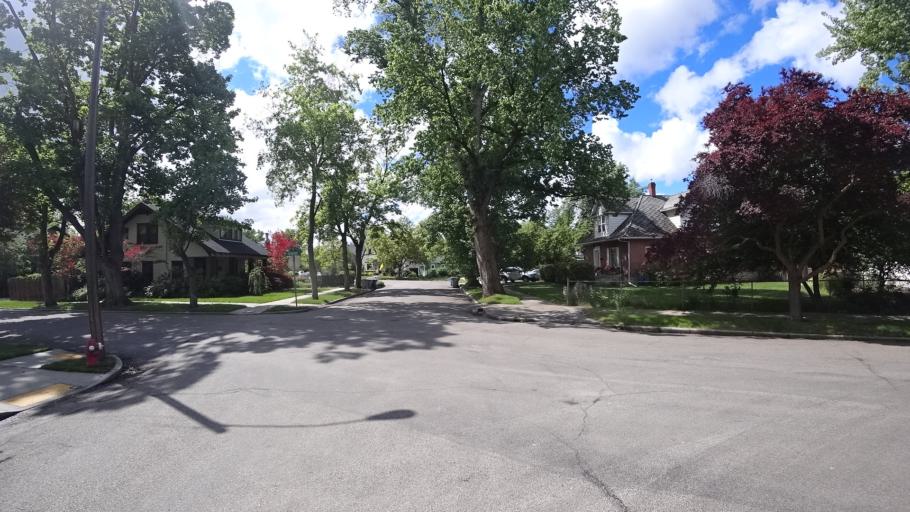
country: US
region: Idaho
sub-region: Ada County
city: Boise
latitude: 43.6268
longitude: -116.2134
